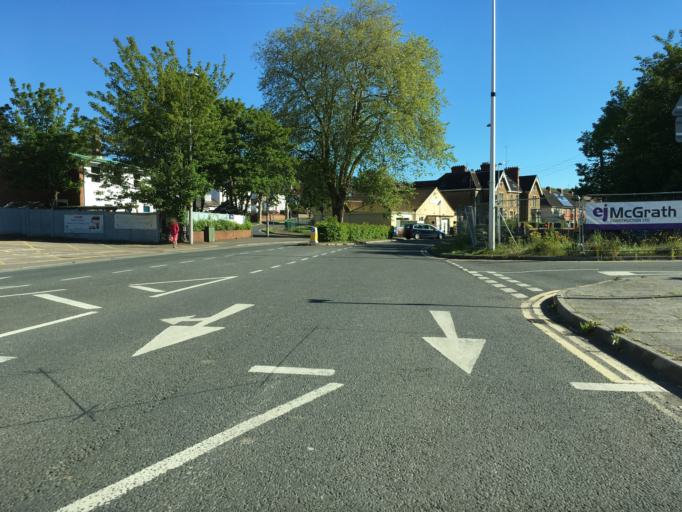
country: GB
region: England
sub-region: North Somerset
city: Portishead
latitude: 51.4861
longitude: -2.7678
